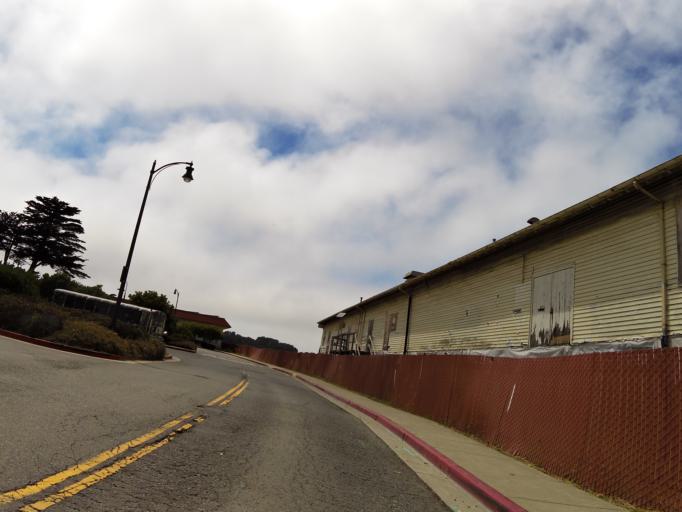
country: US
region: California
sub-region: San Francisco County
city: San Francisco
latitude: 37.8024
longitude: -122.4551
